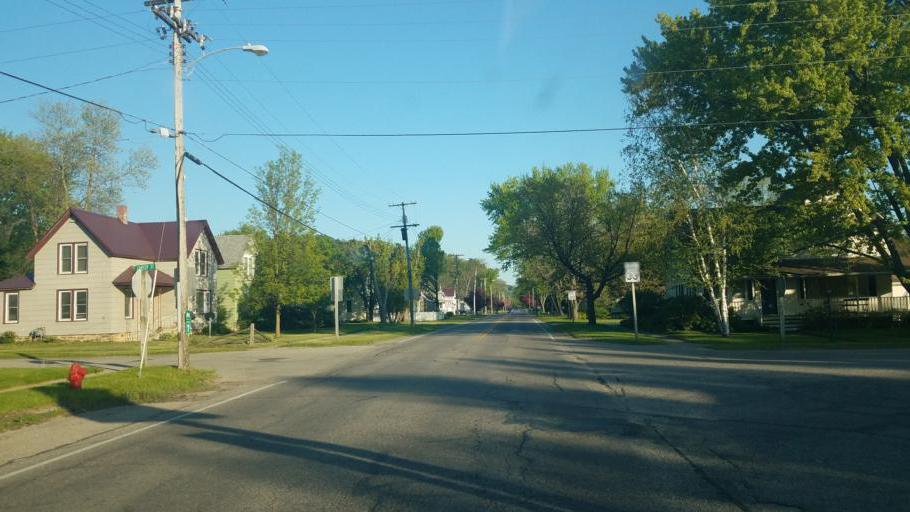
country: US
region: Wisconsin
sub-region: Juneau County
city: Elroy
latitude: 43.6469
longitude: -90.2206
